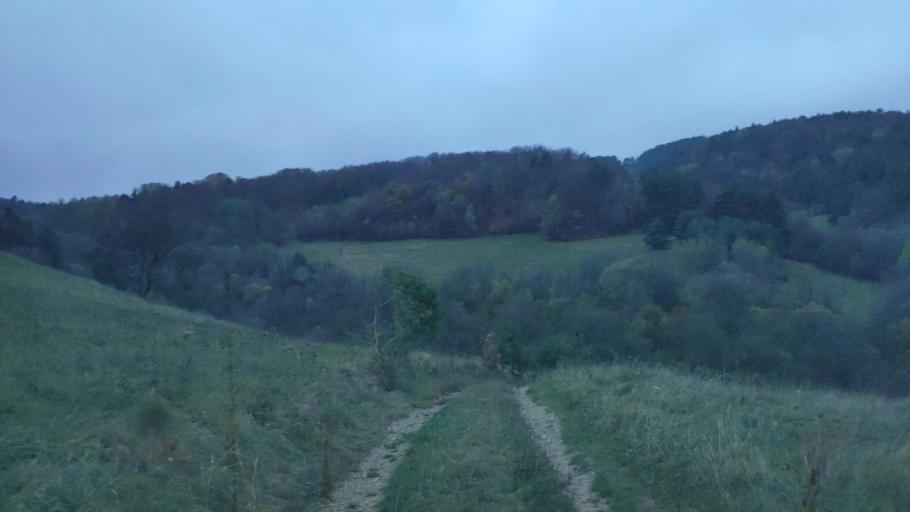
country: SK
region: Presovsky
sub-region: Okres Presov
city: Presov
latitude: 48.9393
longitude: 21.0810
